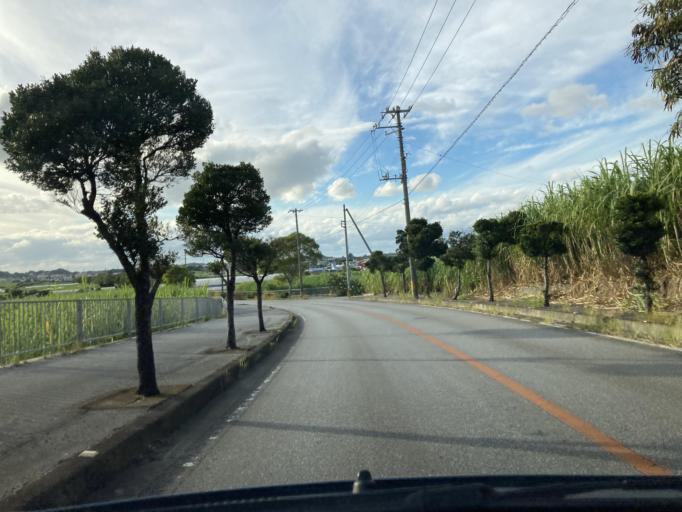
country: JP
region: Okinawa
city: Itoman
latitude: 26.1348
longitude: 127.7215
